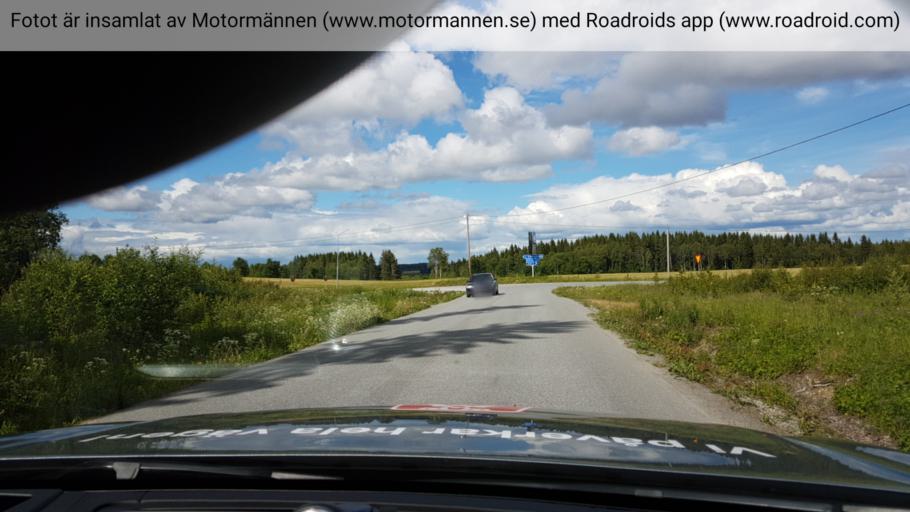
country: SE
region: Jaemtland
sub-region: Bergs Kommun
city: Hoverberg
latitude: 62.9151
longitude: 14.3174
